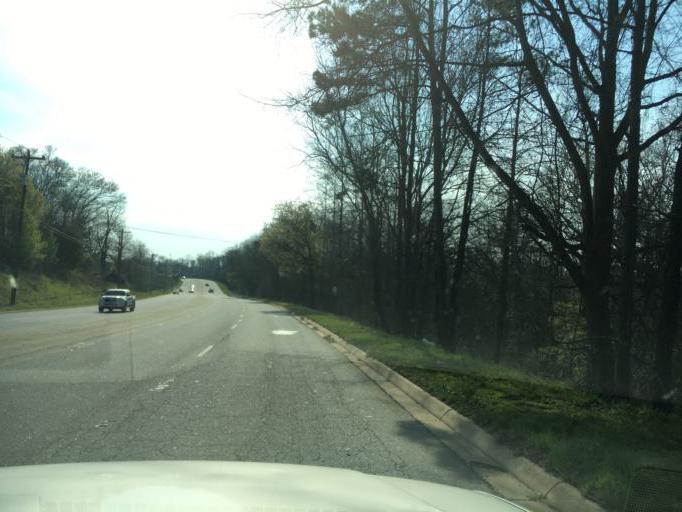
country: US
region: South Carolina
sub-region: Spartanburg County
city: Mayo
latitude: 35.0769
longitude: -81.8689
